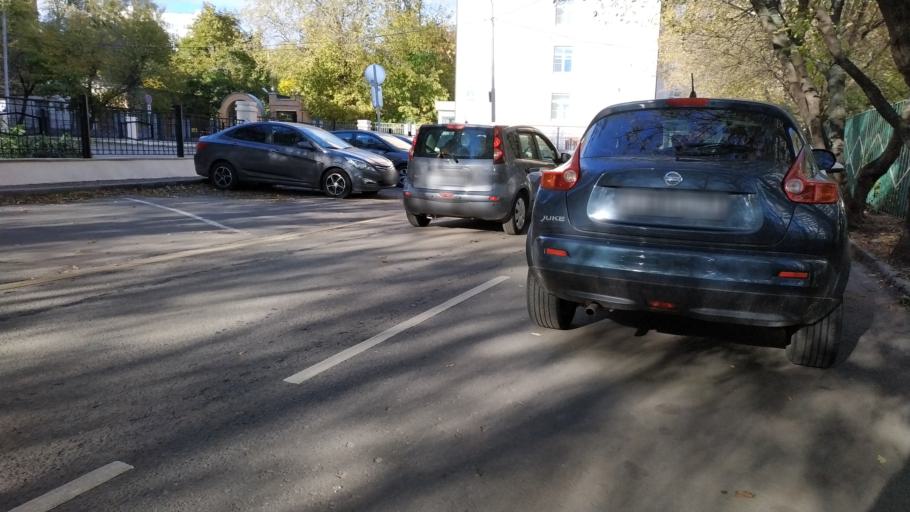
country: RU
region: Moskovskaya
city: Koptevo
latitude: 55.8098
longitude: 37.5287
